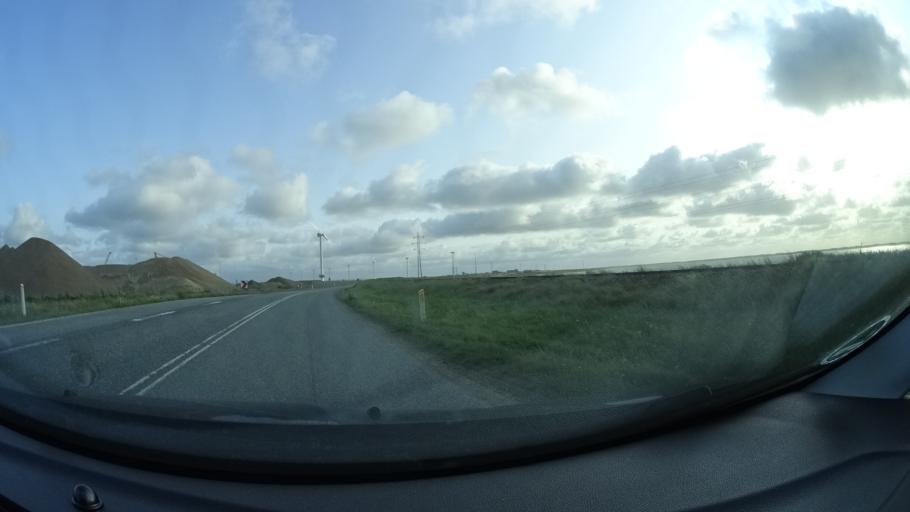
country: DK
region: Central Jutland
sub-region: Lemvig Kommune
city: Thyboron
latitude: 56.6820
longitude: 8.2239
